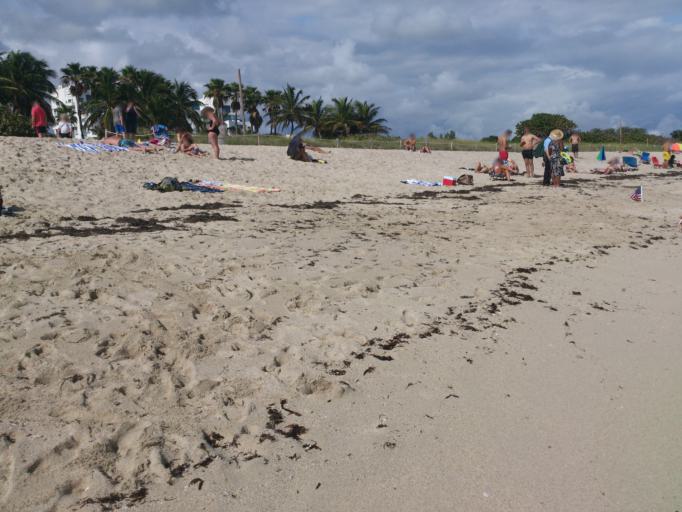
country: US
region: Florida
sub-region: Miami-Dade County
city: Surfside
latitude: 25.8604
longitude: -80.1190
